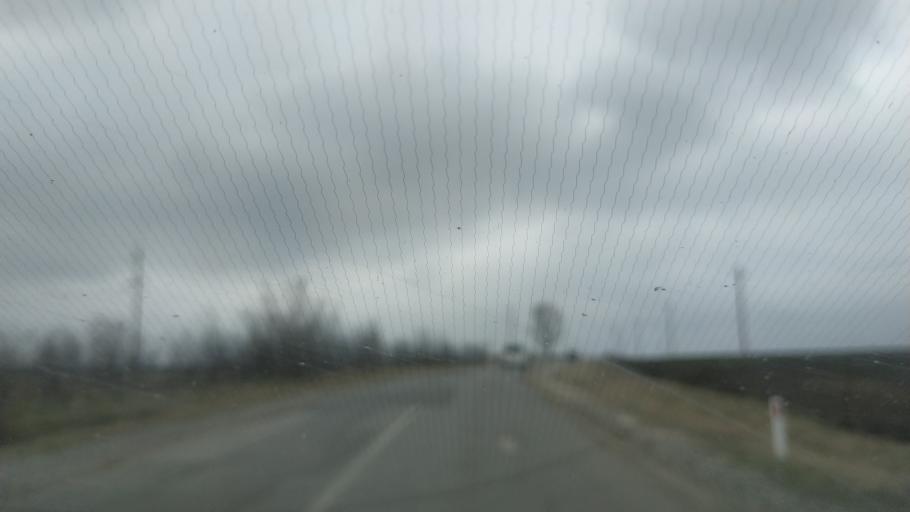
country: MD
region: Gagauzia
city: Bugeac
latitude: 46.3342
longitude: 28.7506
